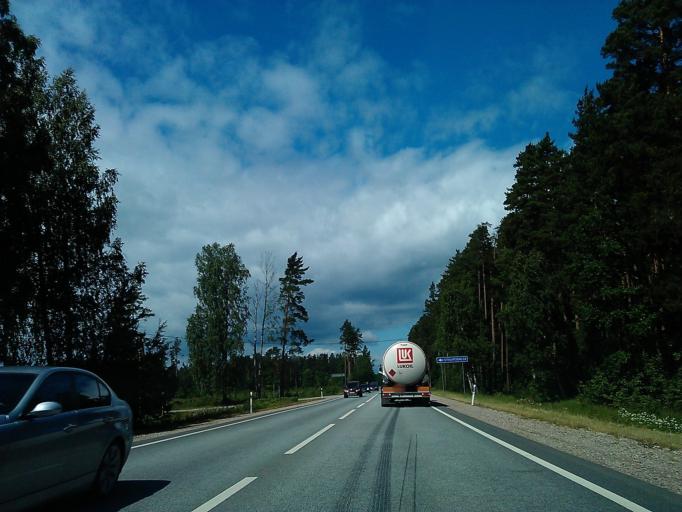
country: LV
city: Tireli
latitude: 56.9275
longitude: 23.6590
